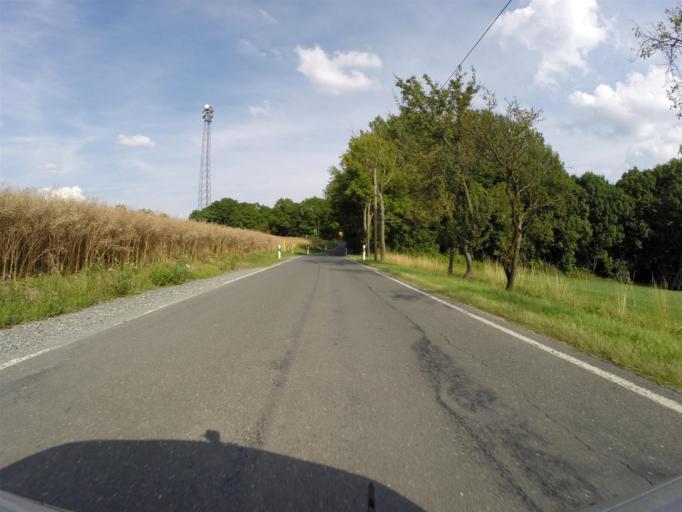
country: DE
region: Thuringia
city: Lehesten
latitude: 50.9703
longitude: 11.5963
